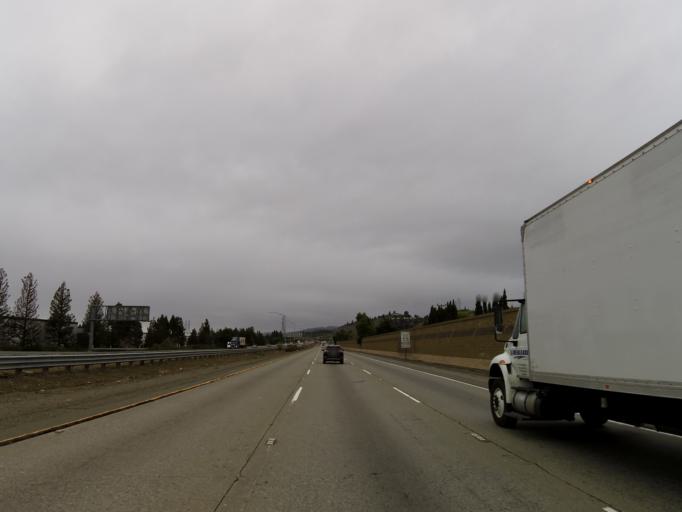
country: US
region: California
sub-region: Alameda County
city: Fremont
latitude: 37.5075
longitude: -121.9353
